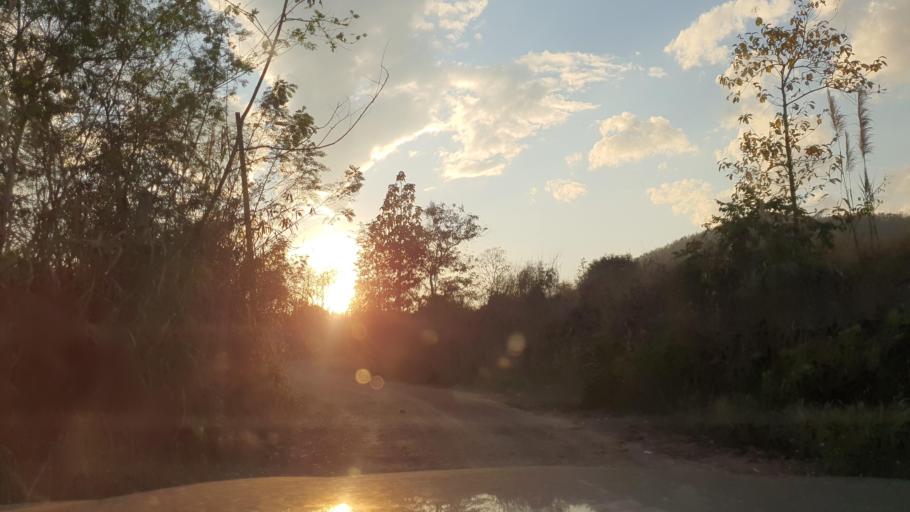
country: TH
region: Chiang Mai
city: Hang Dong
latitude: 18.7356
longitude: 98.8808
